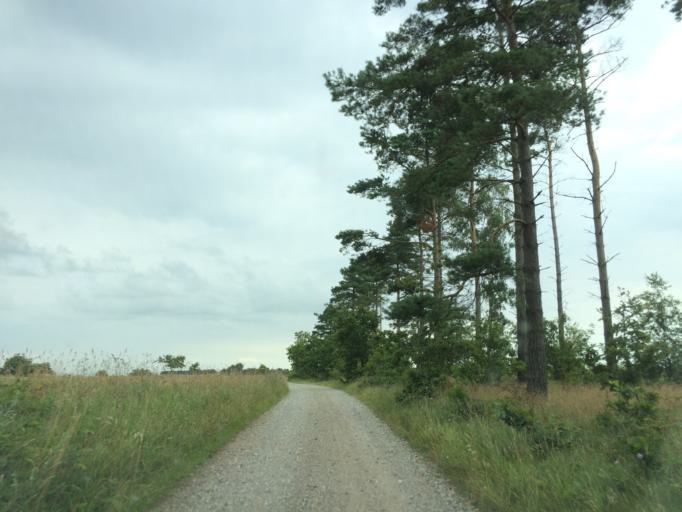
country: DK
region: Central Jutland
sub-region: Syddjurs Kommune
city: Ronde
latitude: 56.2302
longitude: 10.5445
